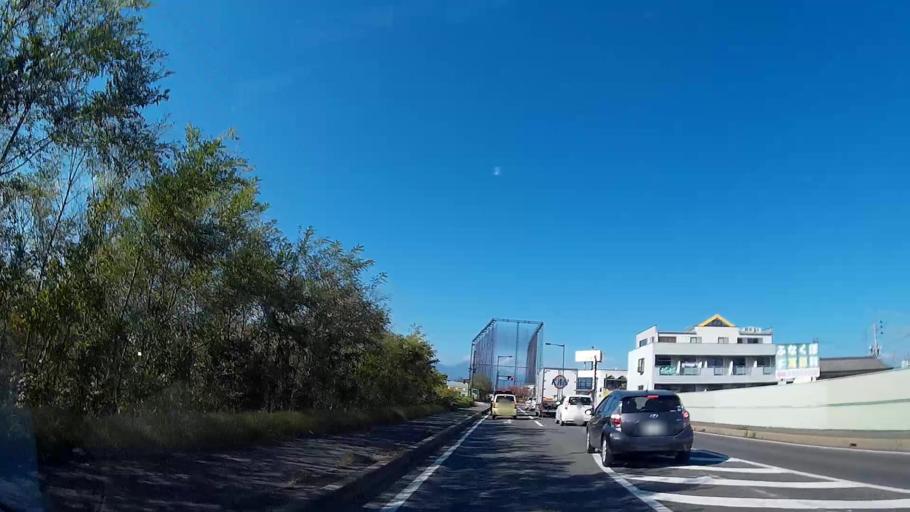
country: JP
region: Nagano
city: Matsumoto
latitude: 36.2002
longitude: 137.9489
